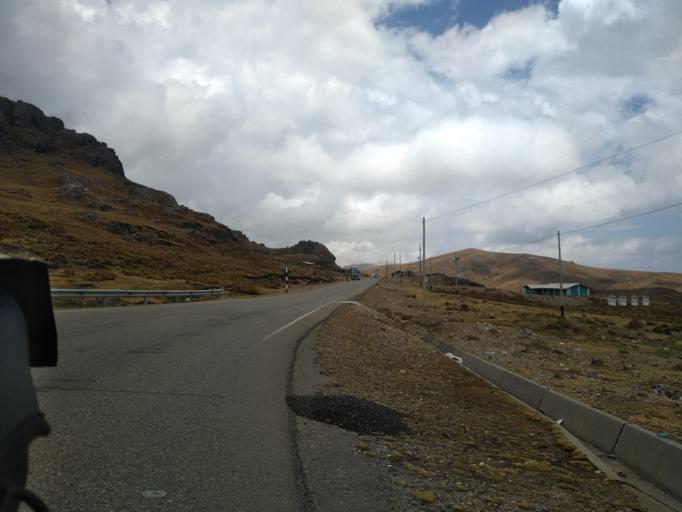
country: PE
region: La Libertad
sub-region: Provincia de Santiago de Chuco
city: Quiruvilca
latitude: -7.9747
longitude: -78.2116
